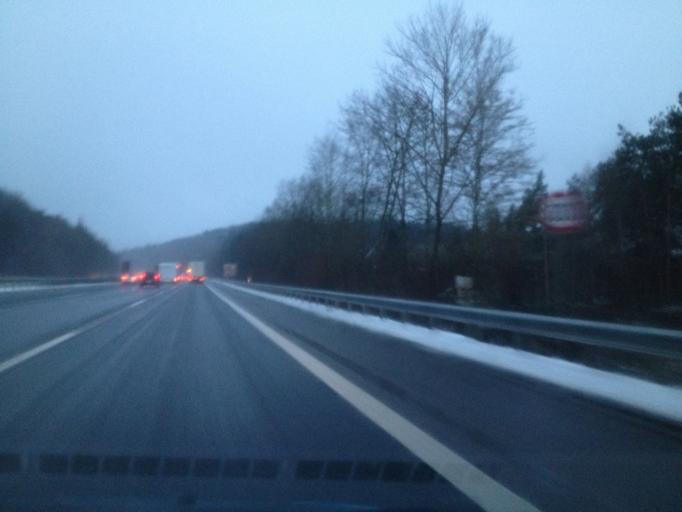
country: DE
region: Rheinland-Pfalz
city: Winningen
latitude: 50.2848
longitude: 7.5095
